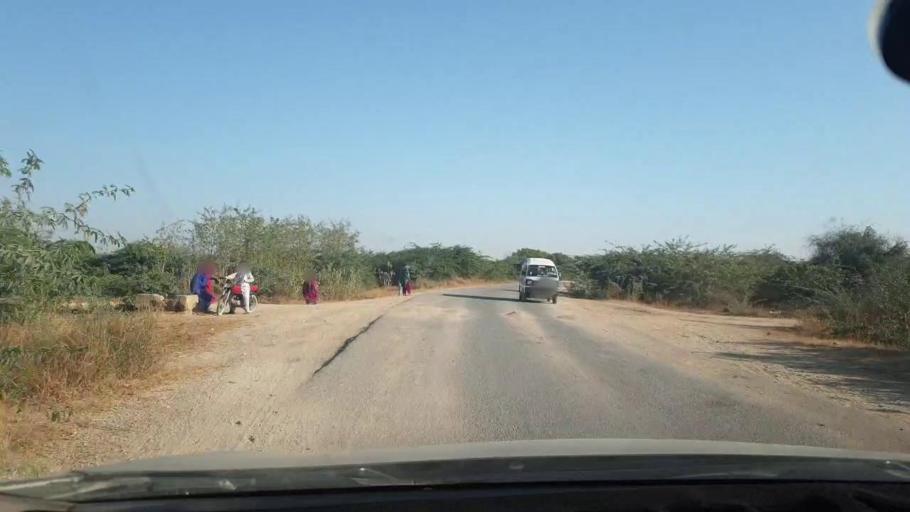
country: PK
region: Sindh
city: Malir Cantonment
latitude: 25.1668
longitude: 67.1969
